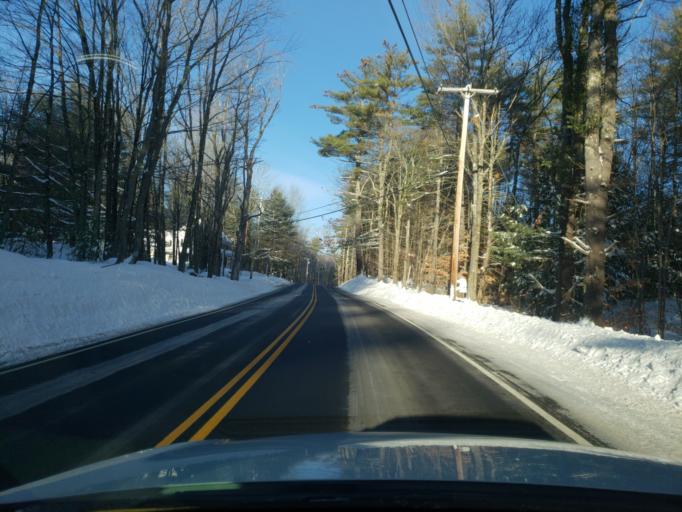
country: US
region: New Hampshire
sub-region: Hillsborough County
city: Greenfield
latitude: 42.9942
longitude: -71.8205
